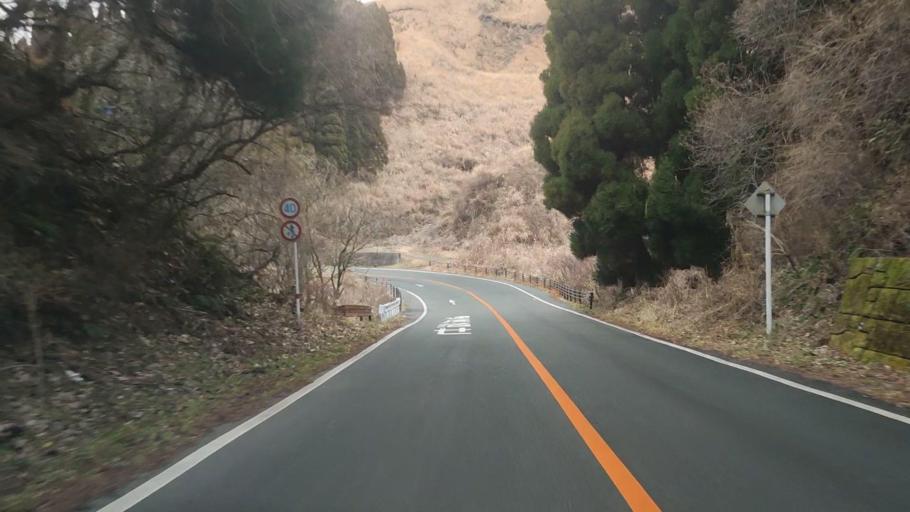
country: JP
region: Kumamoto
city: Aso
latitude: 32.9070
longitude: 131.1444
